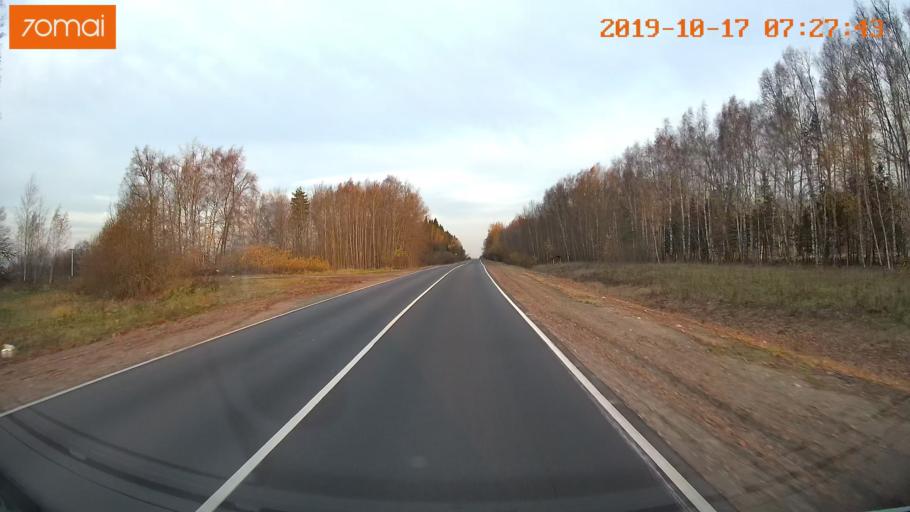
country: RU
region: Ivanovo
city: Gavrilov Posad
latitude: 56.3635
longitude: 40.0698
